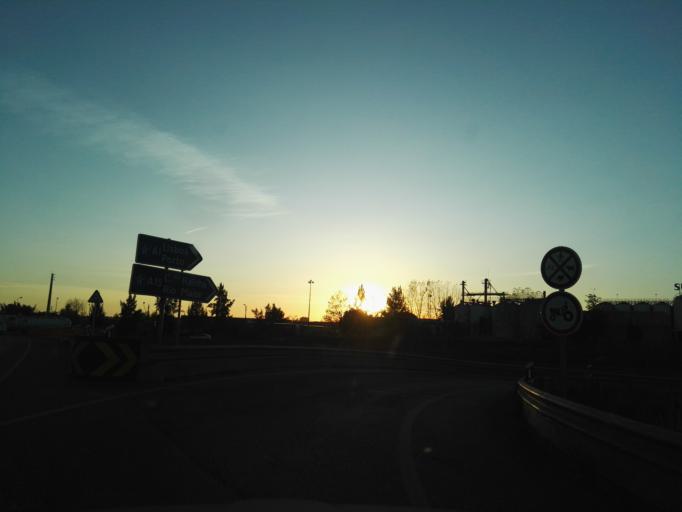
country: PT
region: Santarem
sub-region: Santarem
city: Santarem
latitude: 39.2601
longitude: -8.7039
